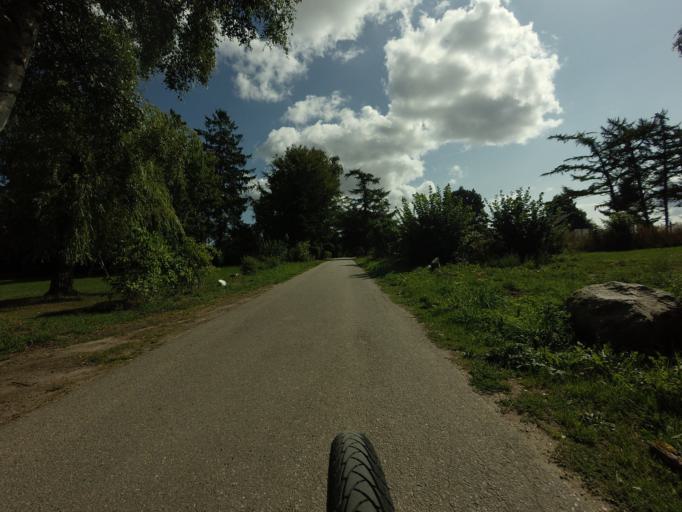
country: DK
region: Zealand
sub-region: Vordingborg Kommune
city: Stege
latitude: 54.9641
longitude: 12.4040
